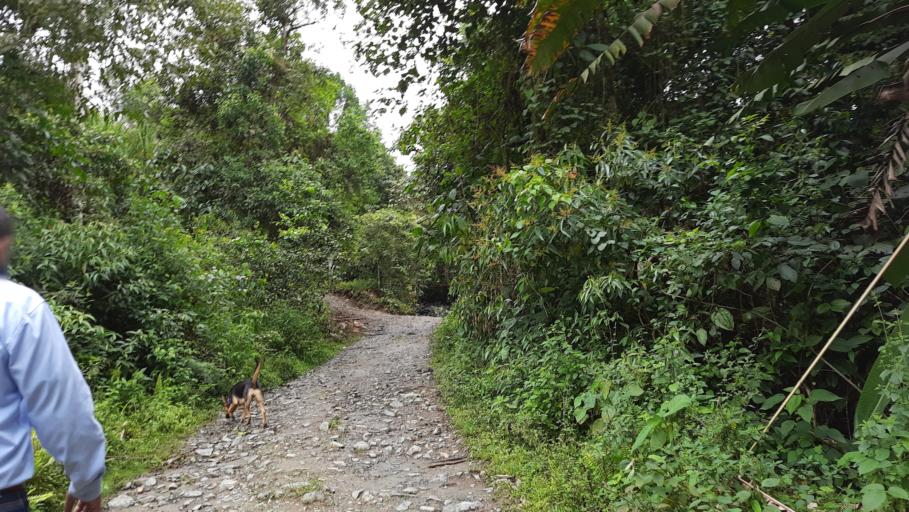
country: CO
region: Valle del Cauca
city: Buga
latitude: 3.8549
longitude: -76.1883
